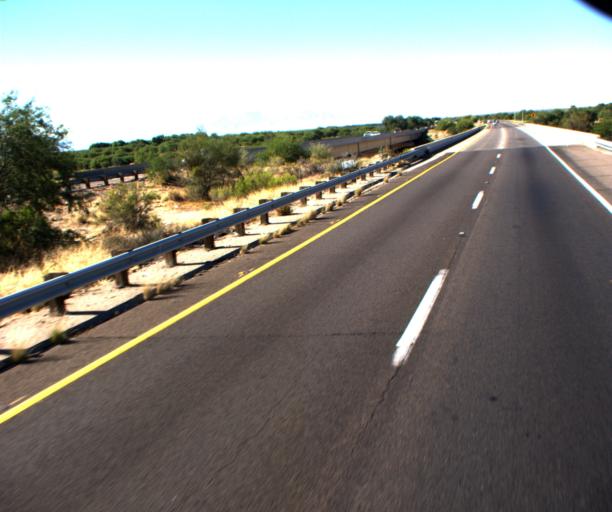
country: US
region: Arizona
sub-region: Pima County
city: Drexel Heights
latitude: 32.1054
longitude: -110.9932
